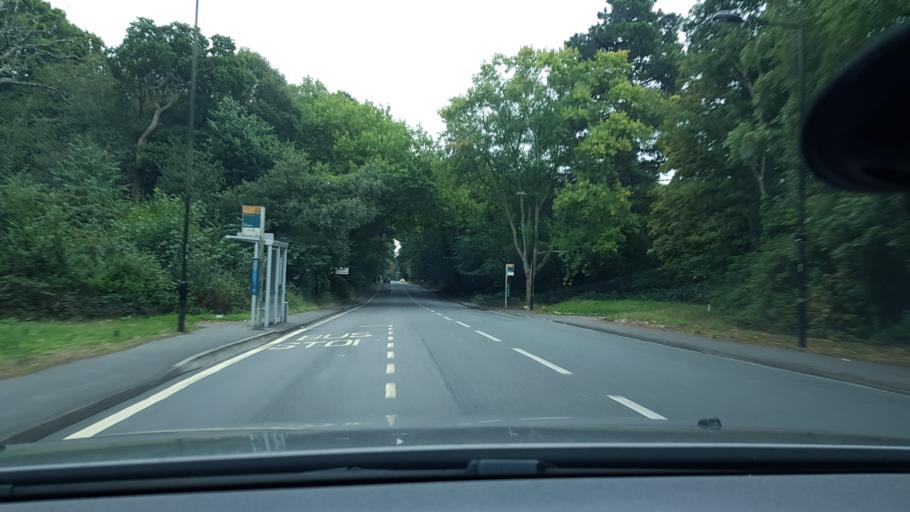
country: GB
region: England
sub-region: Southampton
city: Southampton
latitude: 50.9302
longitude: -1.4058
